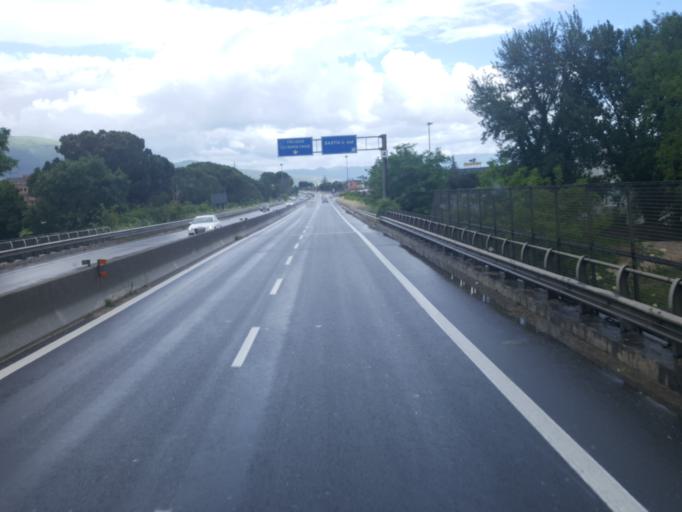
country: IT
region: Umbria
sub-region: Provincia di Perugia
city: Bastia umbra
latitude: 43.0634
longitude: 12.5437
